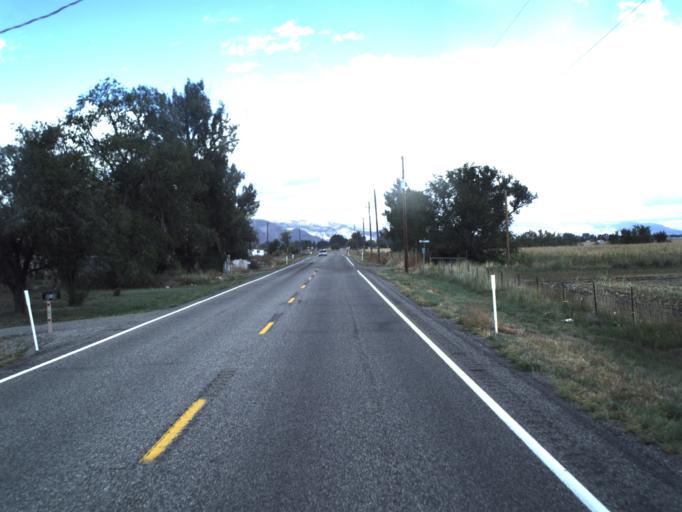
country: US
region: Utah
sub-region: Sevier County
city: Monroe
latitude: 38.6580
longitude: -112.1215
